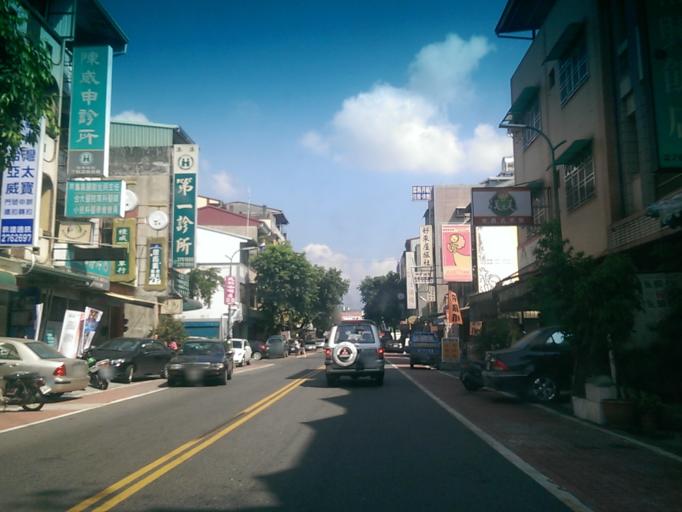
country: TW
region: Taiwan
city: Lugu
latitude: 23.8269
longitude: 120.7821
